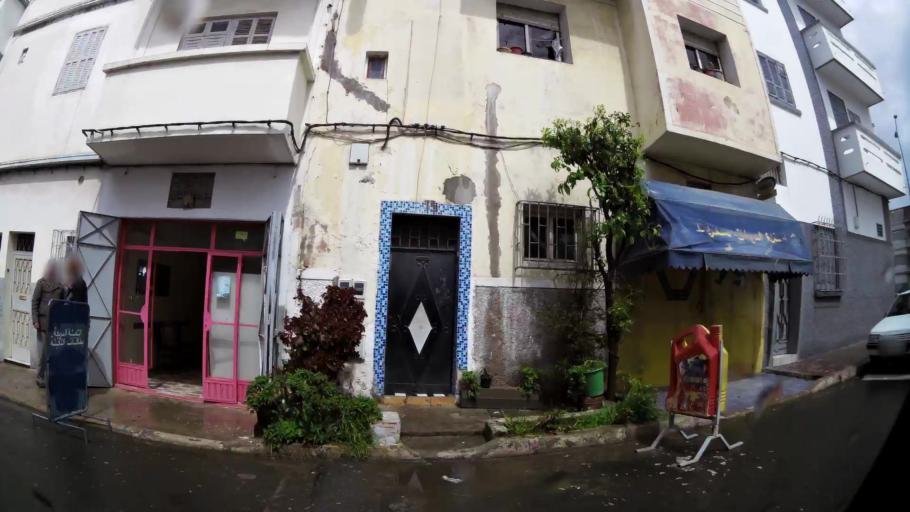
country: MA
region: Grand Casablanca
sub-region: Casablanca
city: Casablanca
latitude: 33.5422
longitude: -7.5656
